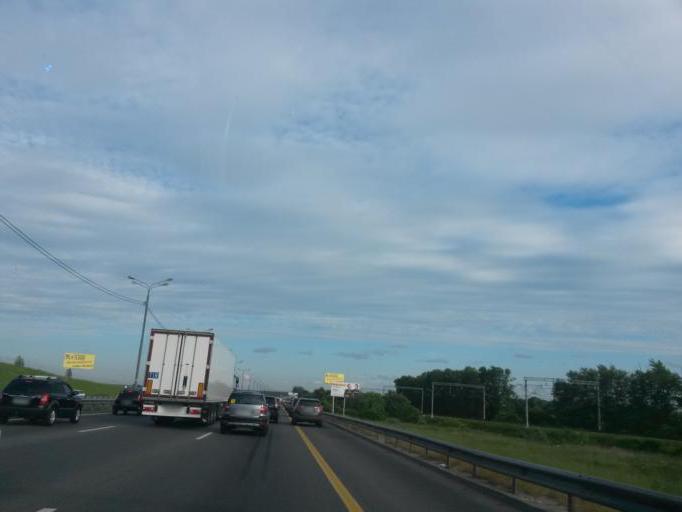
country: RU
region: Moskovskaya
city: Vidnoye
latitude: 55.5138
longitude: 37.7129
